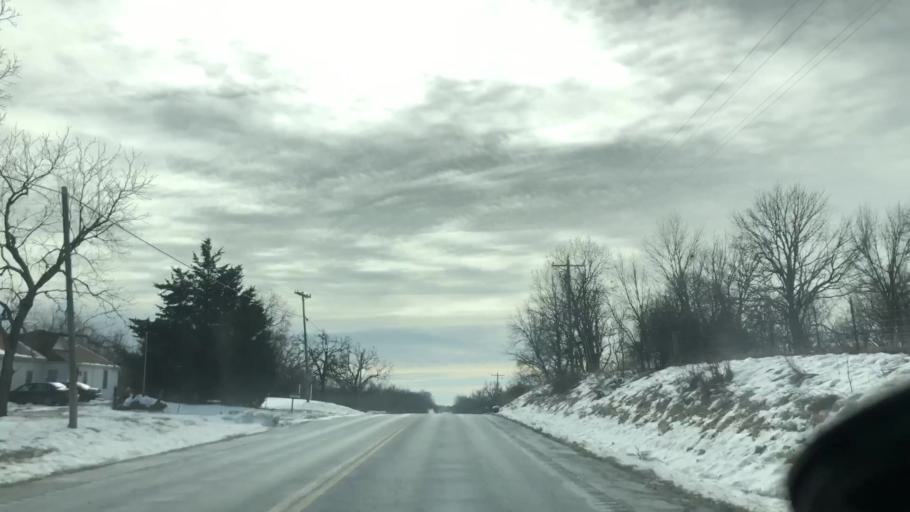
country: US
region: Missouri
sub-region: Jackson County
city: Oak Grove
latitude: 38.9747
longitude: -94.1306
